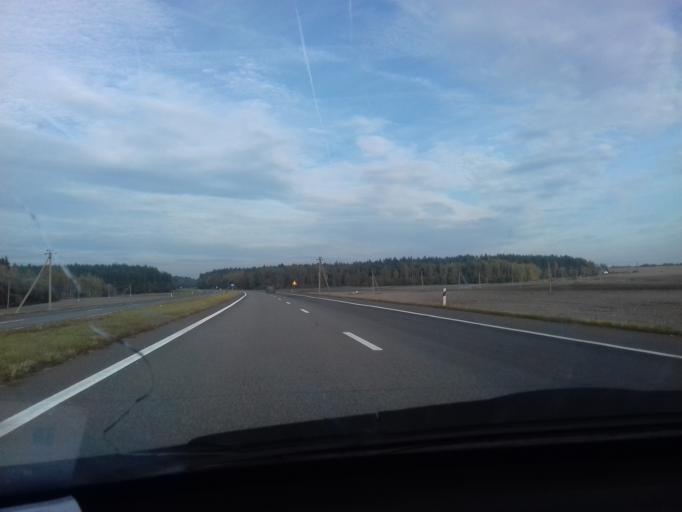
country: BY
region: Minsk
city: Hatava
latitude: 53.7446
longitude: 27.6312
